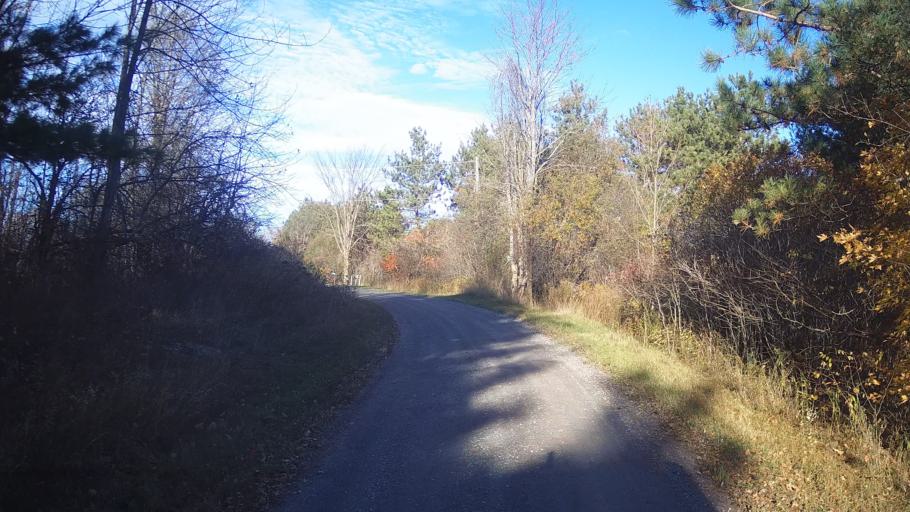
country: CA
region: Ontario
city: Perth
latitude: 44.7368
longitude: -76.4171
